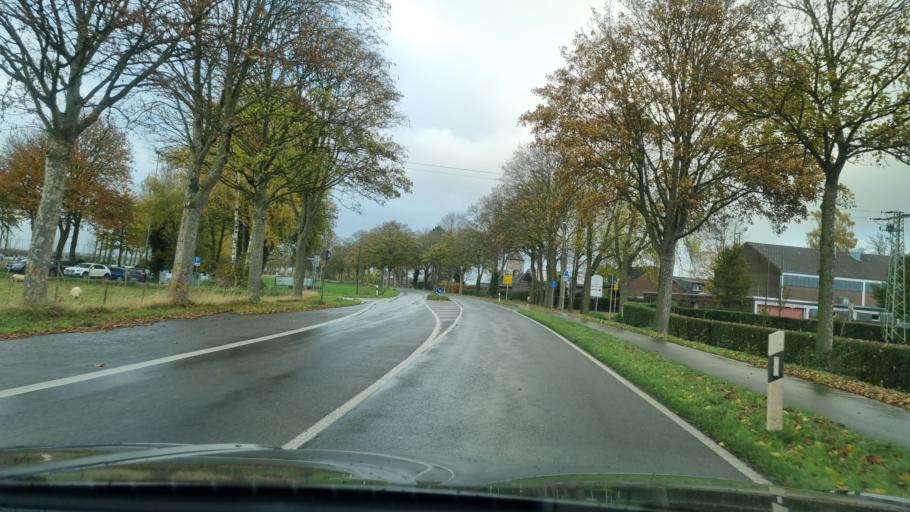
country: DE
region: North Rhine-Westphalia
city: Kalkar
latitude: 51.7869
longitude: 6.3117
